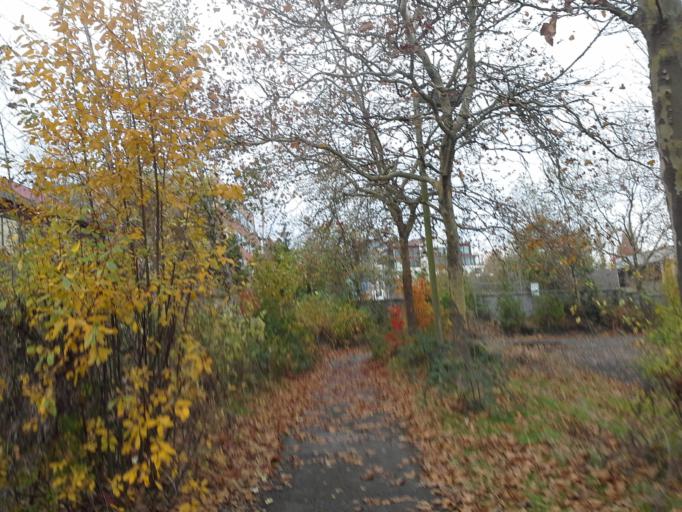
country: US
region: Oregon
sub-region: Multnomah County
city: Portland
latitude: 45.4881
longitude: -122.6728
